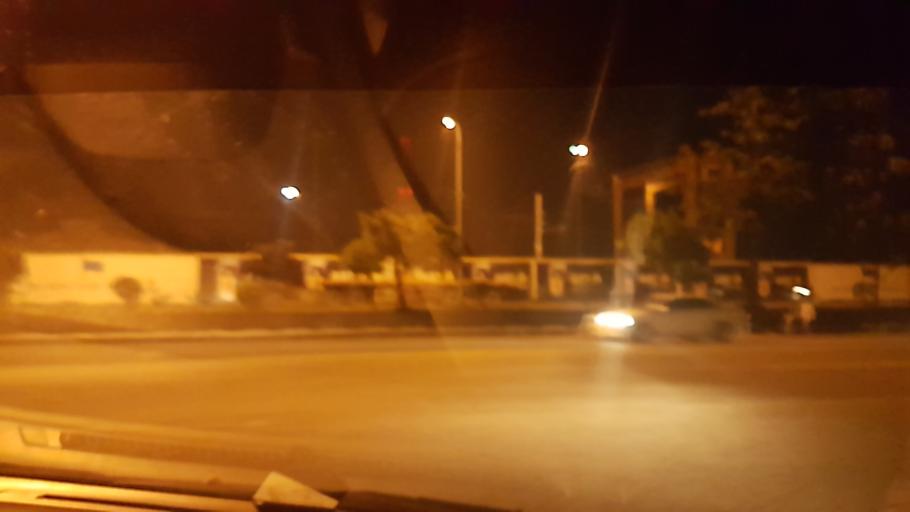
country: MM
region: Yangon
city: Yangon
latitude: 16.7692
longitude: 96.1669
